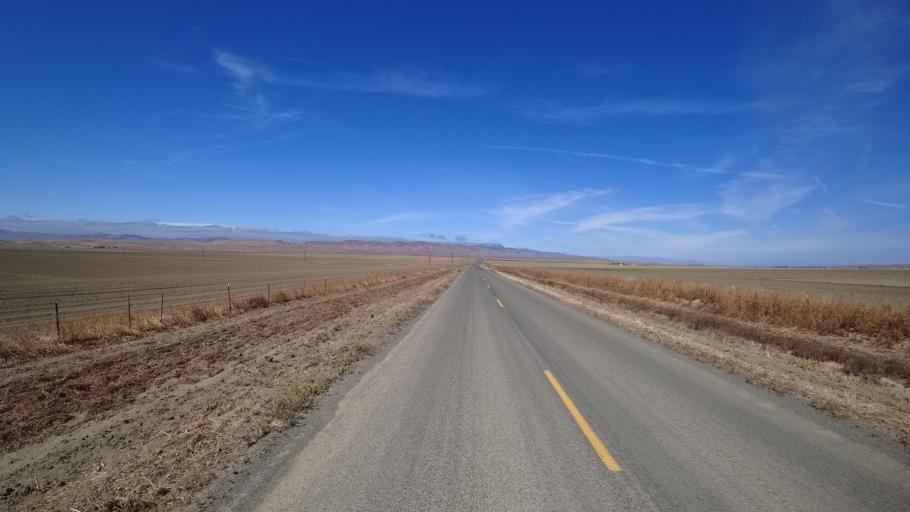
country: US
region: California
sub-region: Kings County
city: Kettleman City
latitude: 35.9351
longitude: -120.0368
